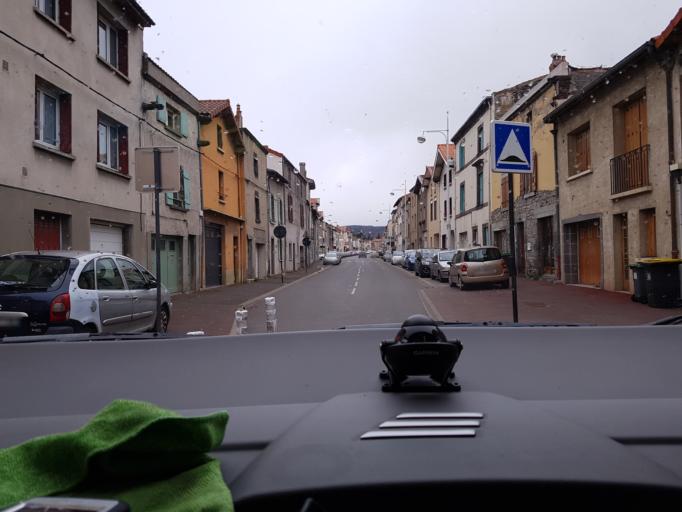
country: FR
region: Auvergne
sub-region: Departement du Puy-de-Dome
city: Mozac
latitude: 45.8936
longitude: 3.0989
